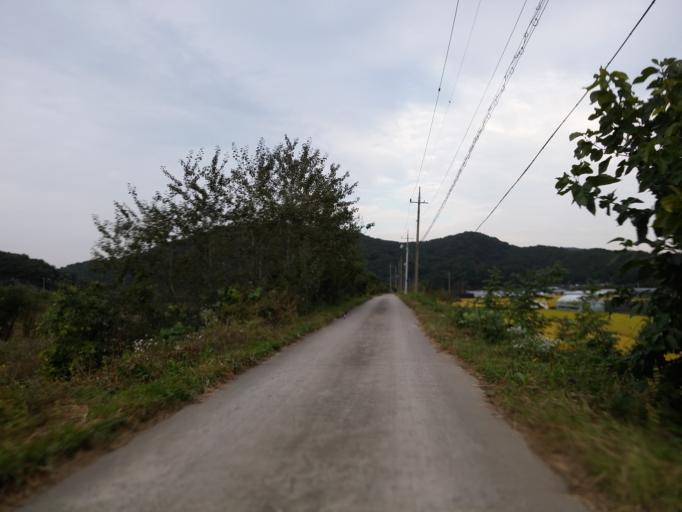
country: KR
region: Daejeon
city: Daejeon
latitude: 36.2509
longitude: 127.3197
